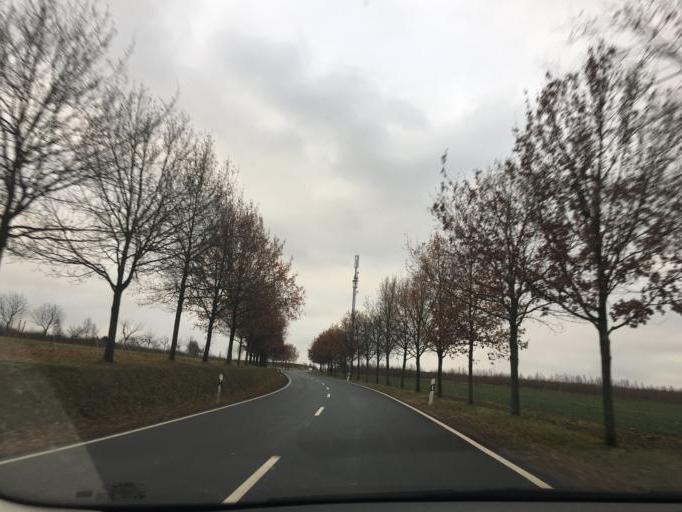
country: DE
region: Saxony
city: Hohenstein-Ernstthal
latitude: 50.8131
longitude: 12.7042
